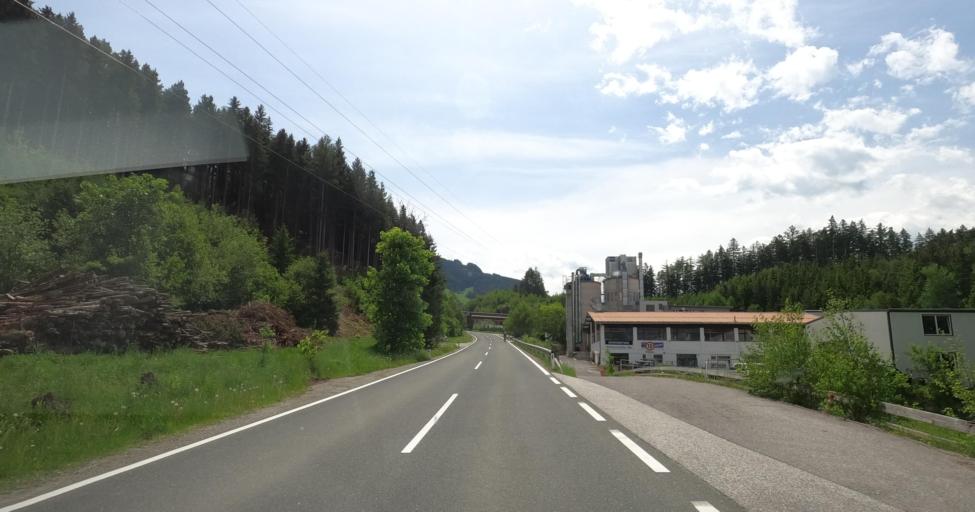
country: AT
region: Tyrol
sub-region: Politischer Bezirk Innsbruck Land
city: Sistrans
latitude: 47.2300
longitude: 11.4300
